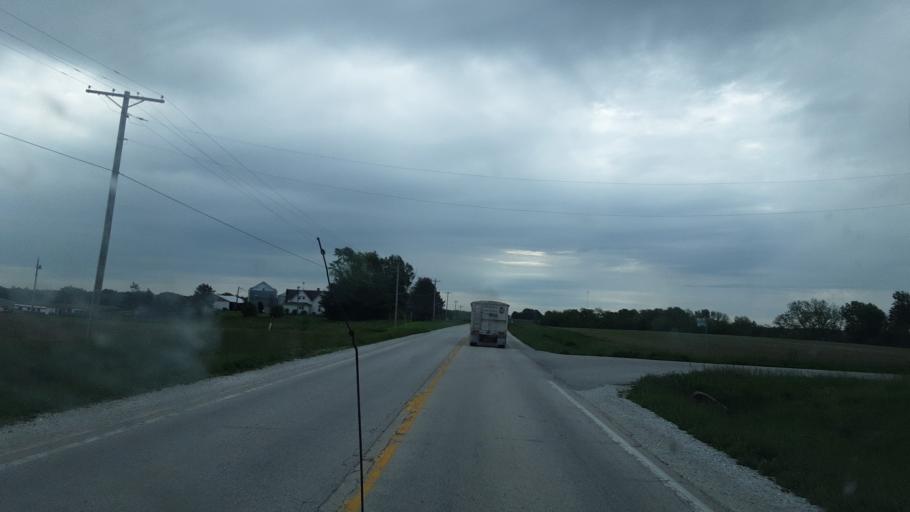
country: US
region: Illinois
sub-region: Fulton County
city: Lewistown
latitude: 40.3426
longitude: -90.2387
